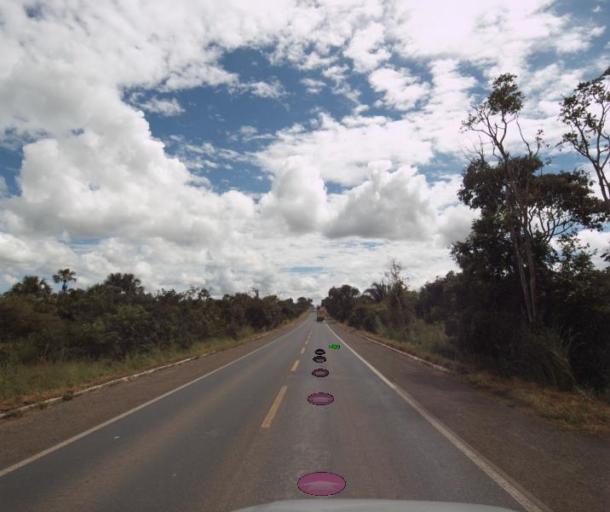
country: BR
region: Goias
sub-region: Uruacu
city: Uruacu
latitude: -14.4450
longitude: -49.1566
